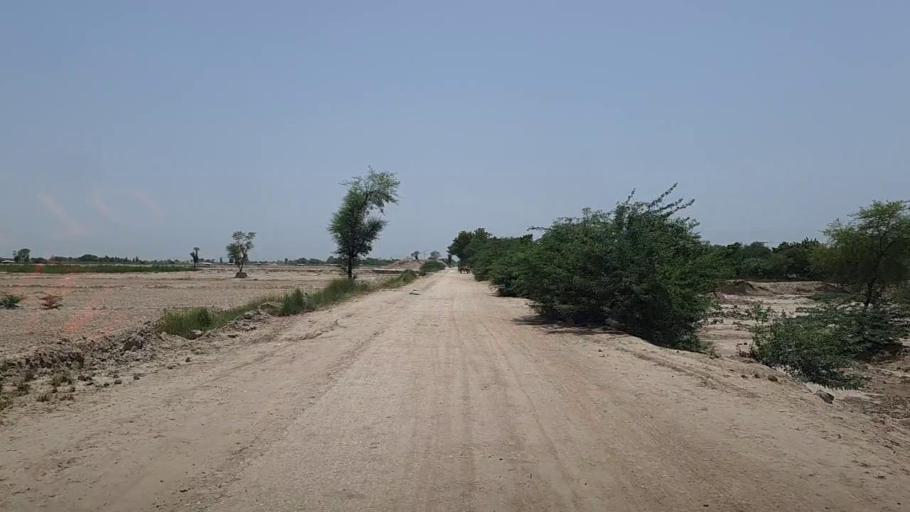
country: PK
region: Sindh
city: Pad Idan
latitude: 26.7671
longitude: 68.2936
